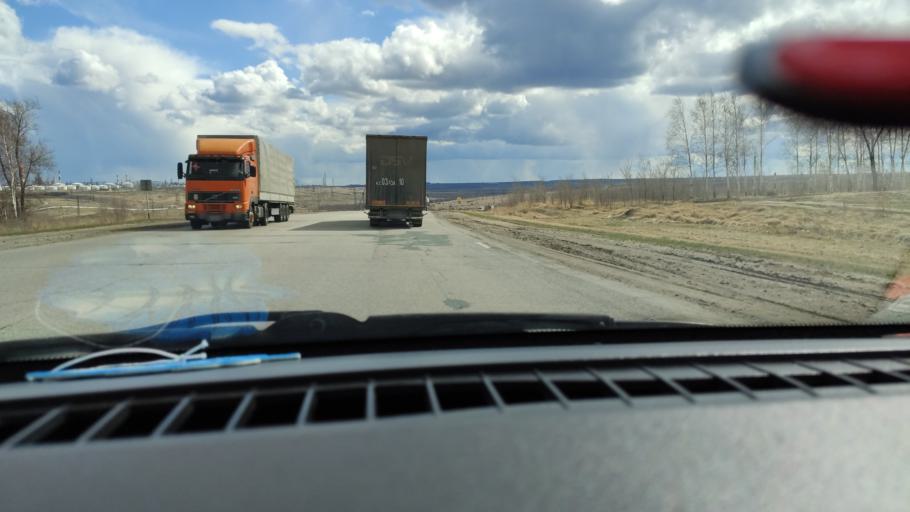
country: RU
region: Samara
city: Varlamovo
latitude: 53.1049
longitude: 48.3568
